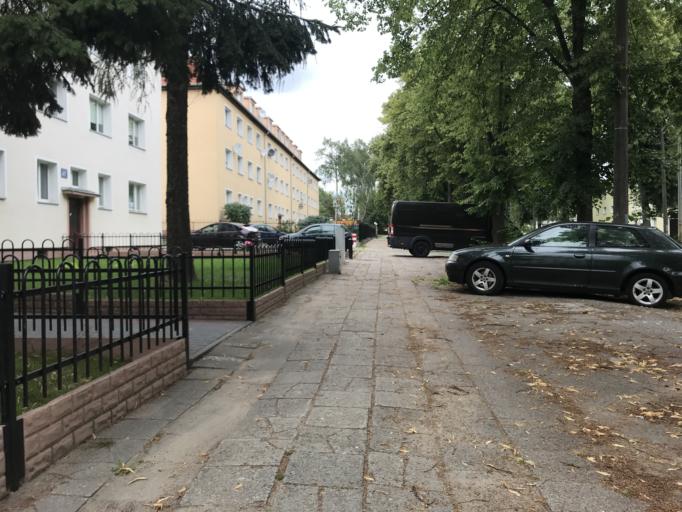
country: PL
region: Warmian-Masurian Voivodeship
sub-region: Powiat elblaski
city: Elblag
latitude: 54.1746
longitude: 19.4177
